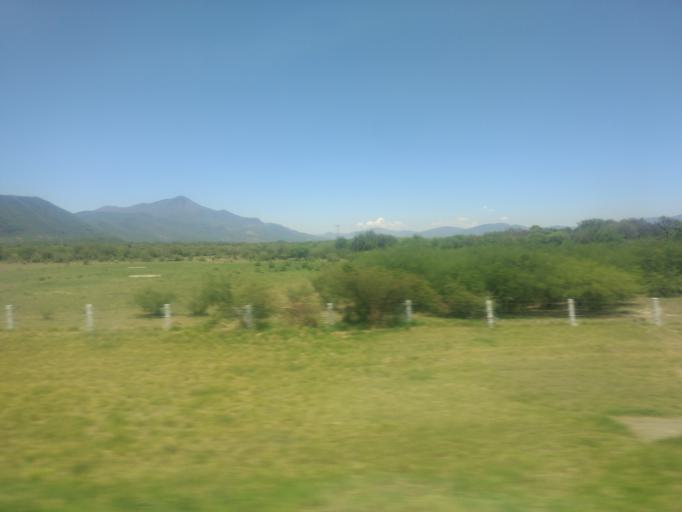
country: MX
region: Jalisco
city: Zacoalco de Torres
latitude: 20.1546
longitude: -103.5020
